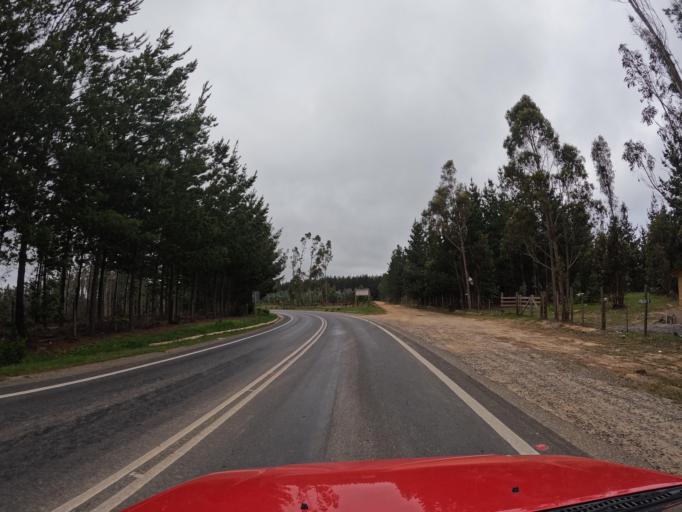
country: CL
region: O'Higgins
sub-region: Provincia de Colchagua
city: Santa Cruz
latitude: -34.5806
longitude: -72.0143
